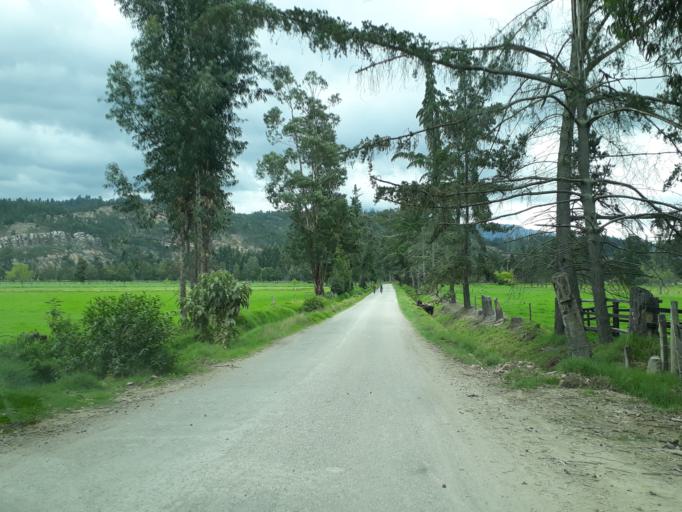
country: CO
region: Cundinamarca
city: Ubate
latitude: 5.2727
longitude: -73.8195
